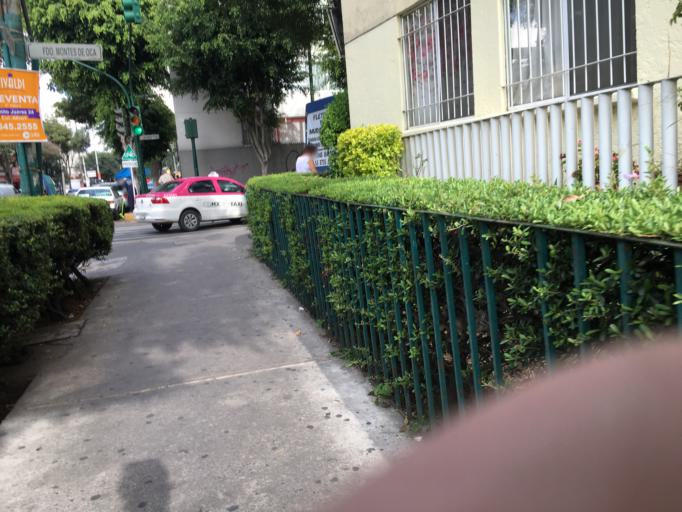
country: MX
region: Mexico City
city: Colonia Nativitas
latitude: 19.3716
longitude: -99.1446
